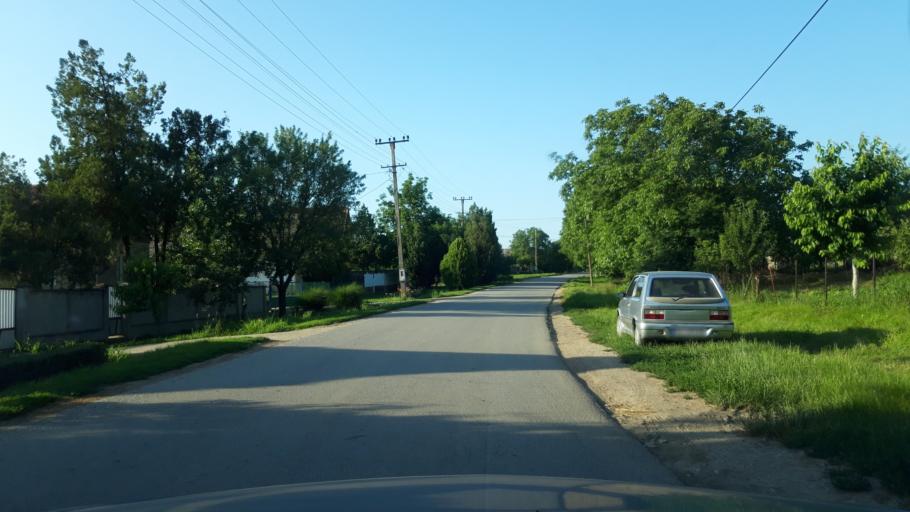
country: RS
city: Celarevo
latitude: 45.1090
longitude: 19.5045
